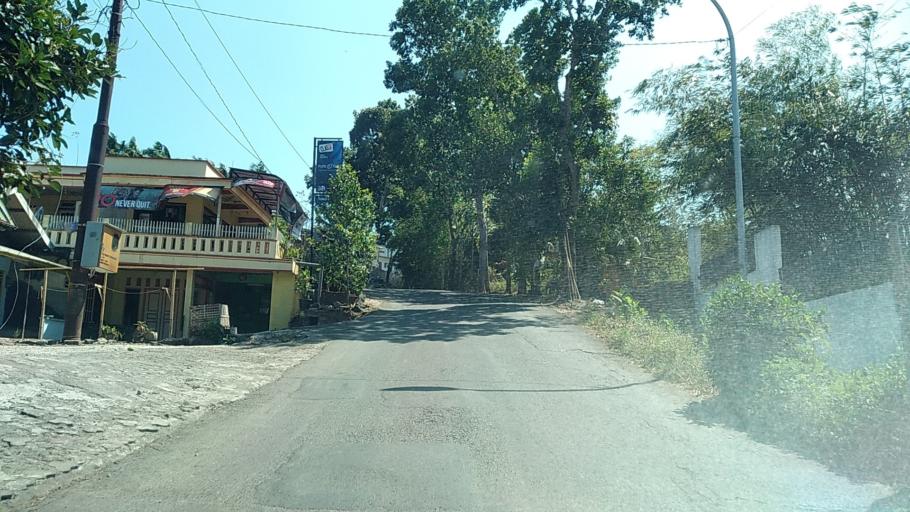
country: ID
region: Central Java
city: Ungaran
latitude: -7.1102
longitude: 110.4039
